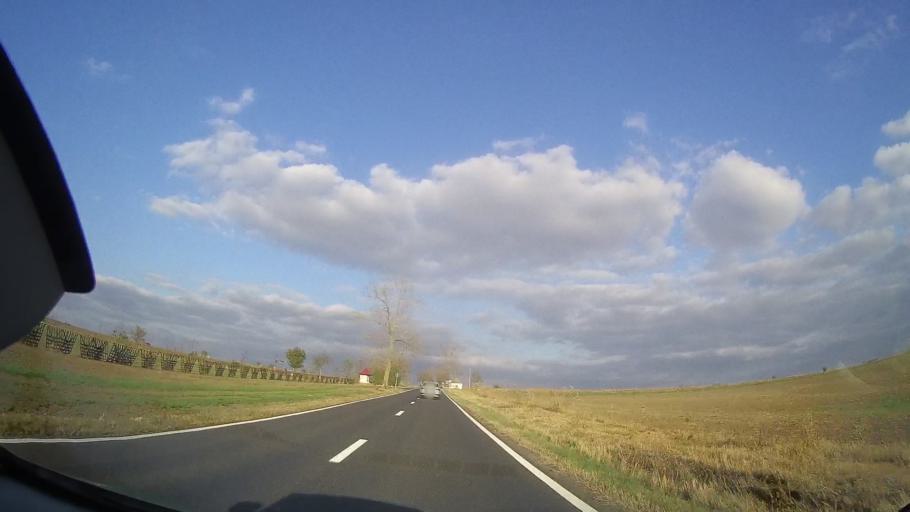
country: RO
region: Tulcea
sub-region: Comuna Topolog
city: Topolog
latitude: 44.8464
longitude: 28.3161
